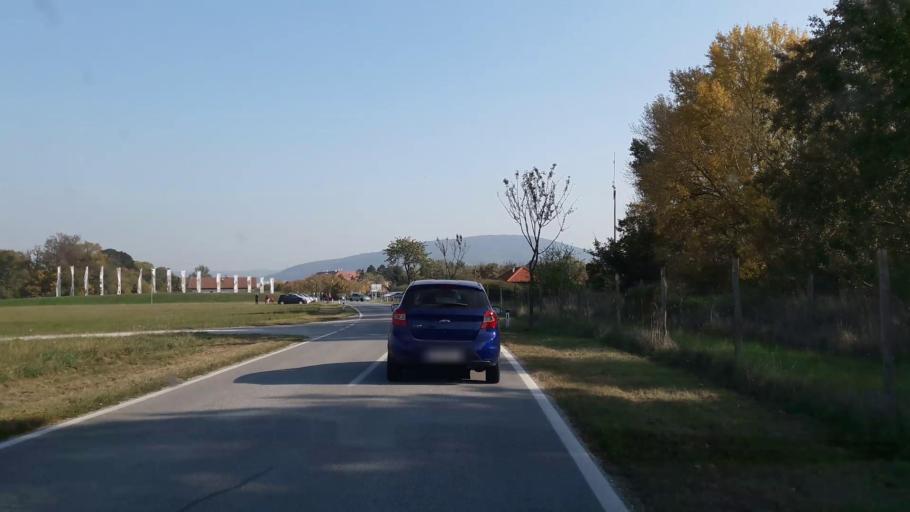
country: AT
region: Lower Austria
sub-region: Politischer Bezirk Ganserndorf
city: Marchegg
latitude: 48.2164
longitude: 16.9273
